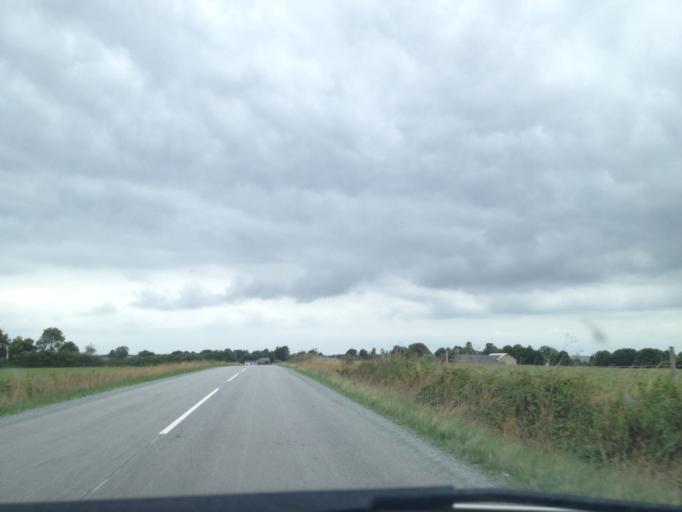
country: DK
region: South Denmark
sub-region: Kolding Kommune
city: Christiansfeld
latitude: 55.3069
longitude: 9.5156
